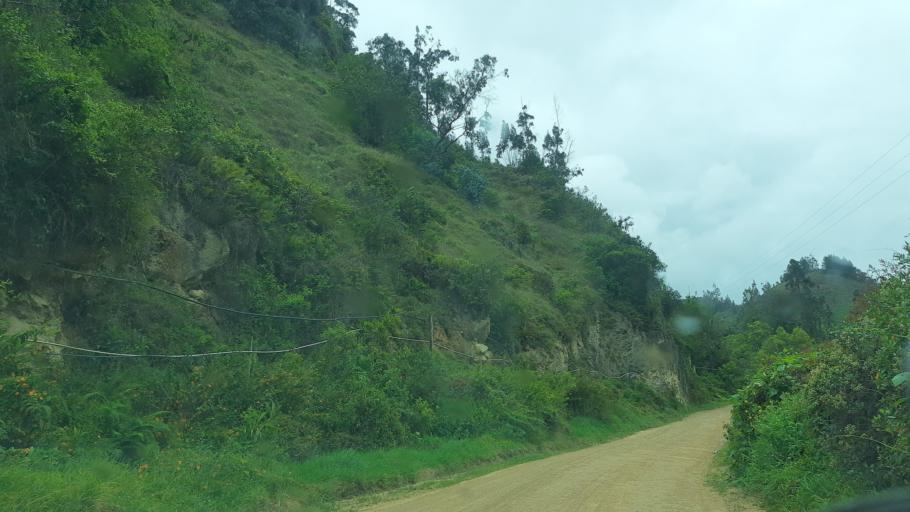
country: CO
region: Boyaca
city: Tibana
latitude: 5.3093
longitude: -73.4332
